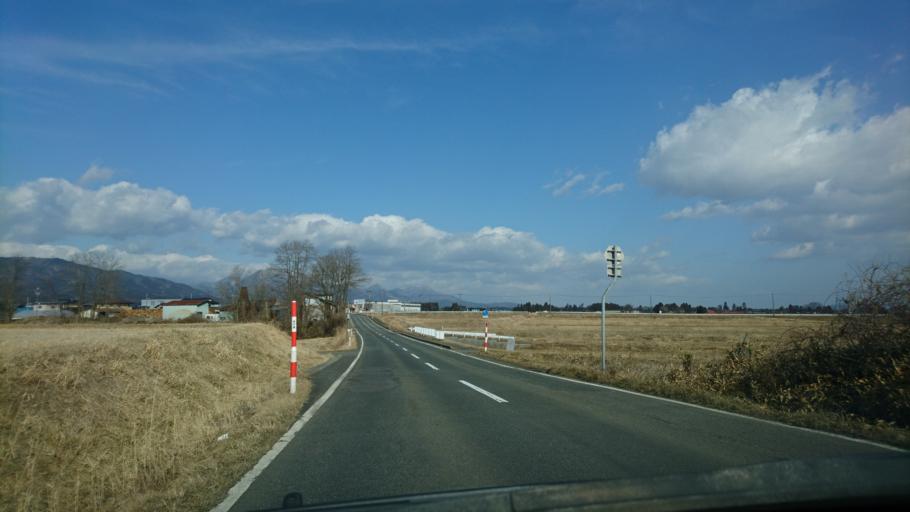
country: JP
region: Iwate
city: Hanamaki
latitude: 39.5101
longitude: 141.1380
